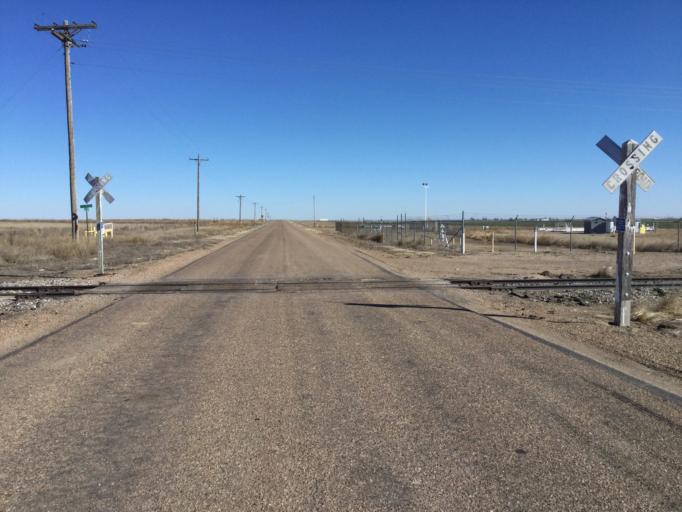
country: US
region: Kansas
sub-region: Grant County
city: Ulysses
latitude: 37.5619
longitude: -101.4901
